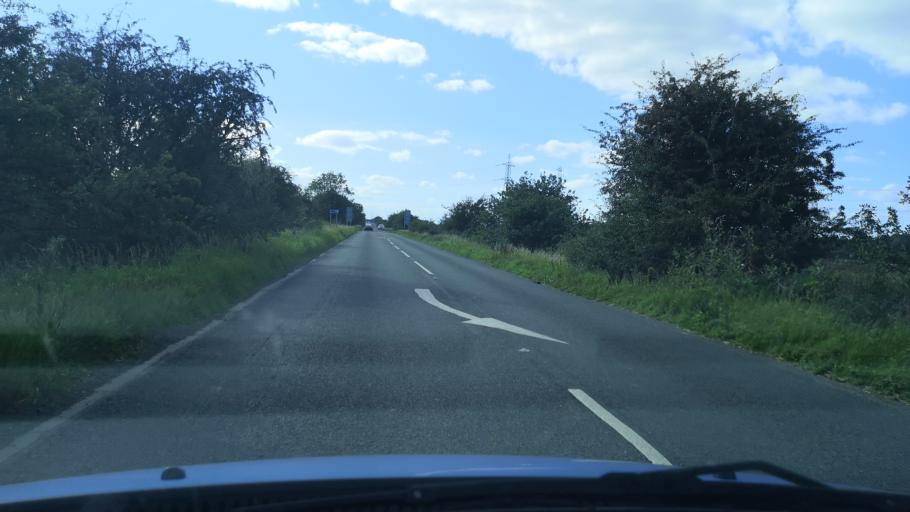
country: GB
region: England
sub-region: Doncaster
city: Kirk Sandall
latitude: 53.5721
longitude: -1.0946
